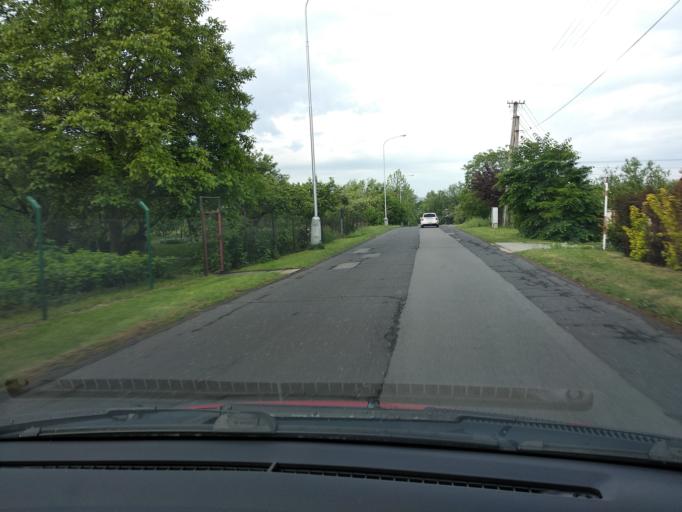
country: CZ
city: Sviadnov
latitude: 49.7009
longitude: 18.3417
